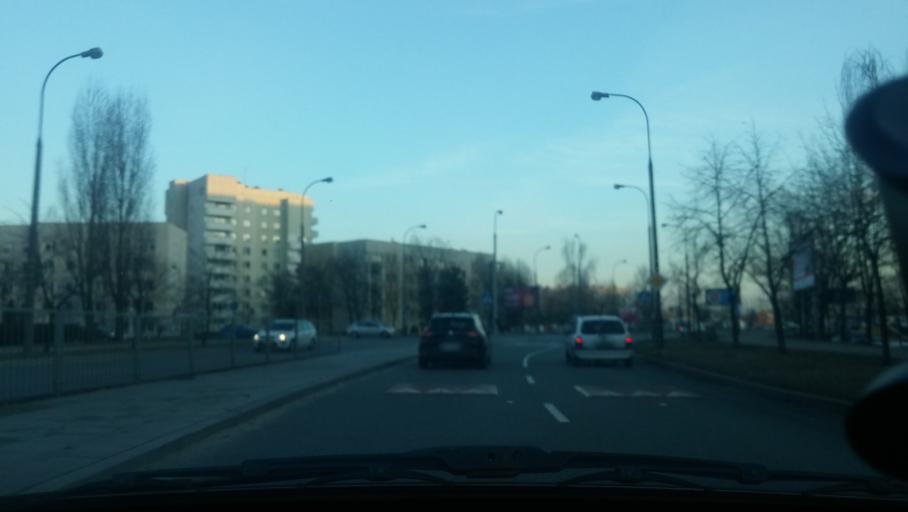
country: PL
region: Masovian Voivodeship
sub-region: Warszawa
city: Praga Poludnie
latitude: 52.2254
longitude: 21.1015
